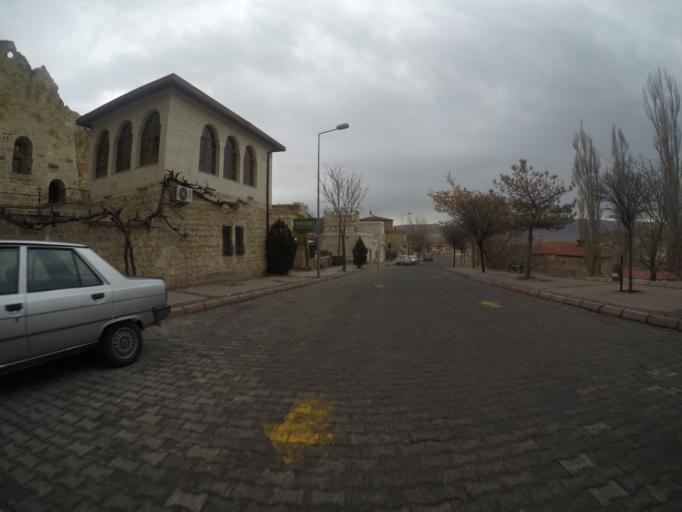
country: TR
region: Nevsehir
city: Urgub
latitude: 38.6333
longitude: 34.9064
